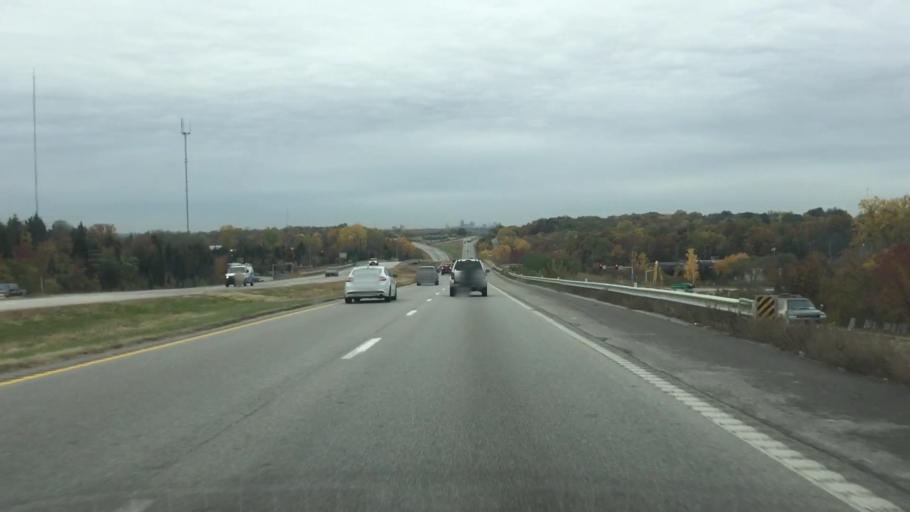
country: US
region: Missouri
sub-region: Jackson County
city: Raytown
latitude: 39.0080
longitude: -94.4873
